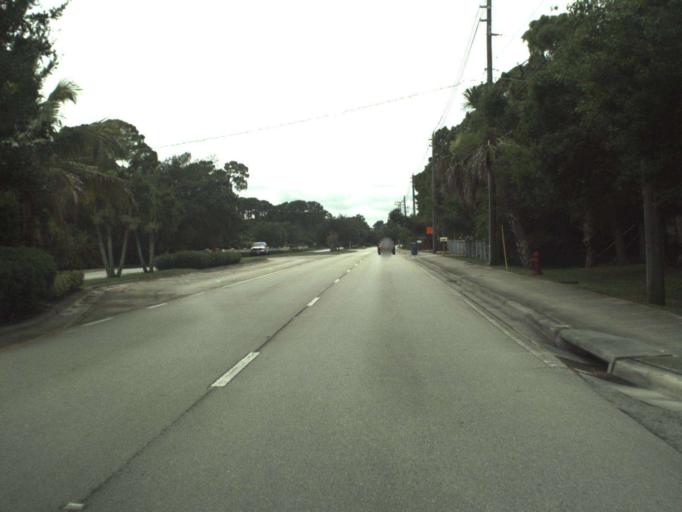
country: US
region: Florida
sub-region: Saint Lucie County
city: White City
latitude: 27.3699
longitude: -80.3504
